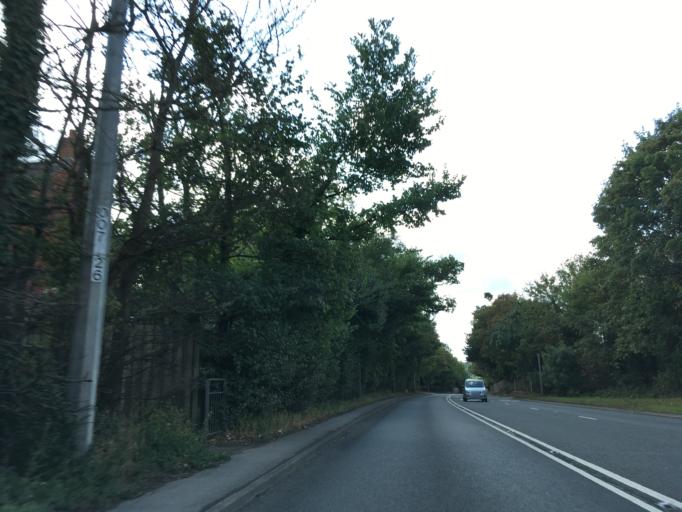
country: GB
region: England
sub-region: West Berkshire
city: Greenham
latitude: 51.3798
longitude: -1.3189
